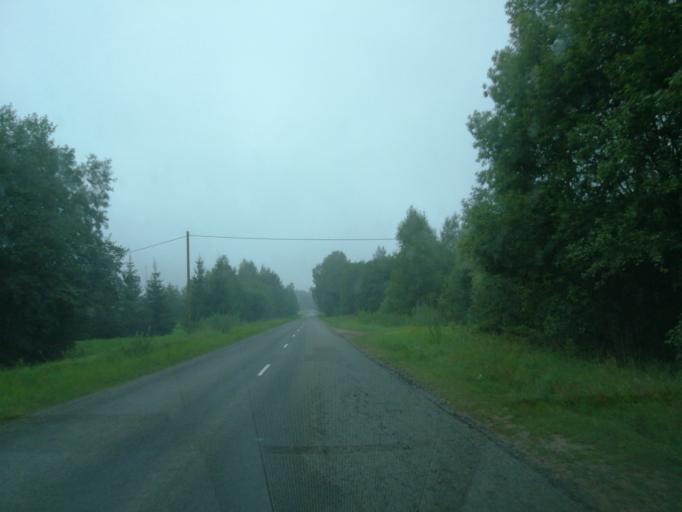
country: LV
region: Preilu Rajons
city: Preili
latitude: 56.2901
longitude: 26.7483
